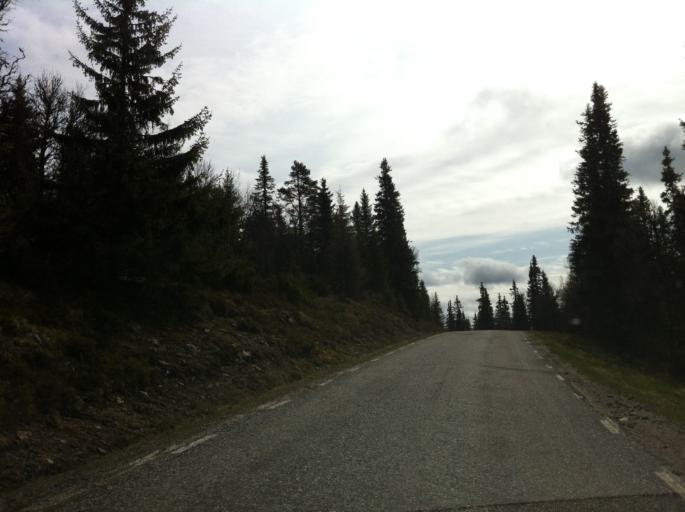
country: NO
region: Hedmark
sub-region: Engerdal
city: Engerdal
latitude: 62.3001
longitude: 12.8028
